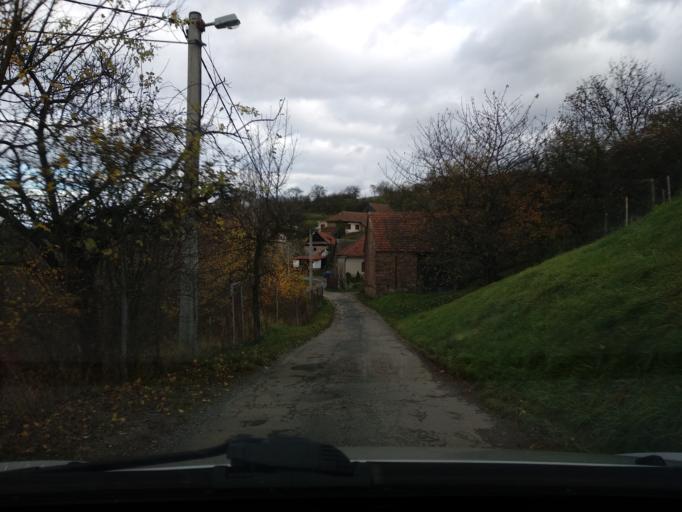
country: CZ
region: South Moravian
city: Drasov
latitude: 49.3729
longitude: 16.4715
